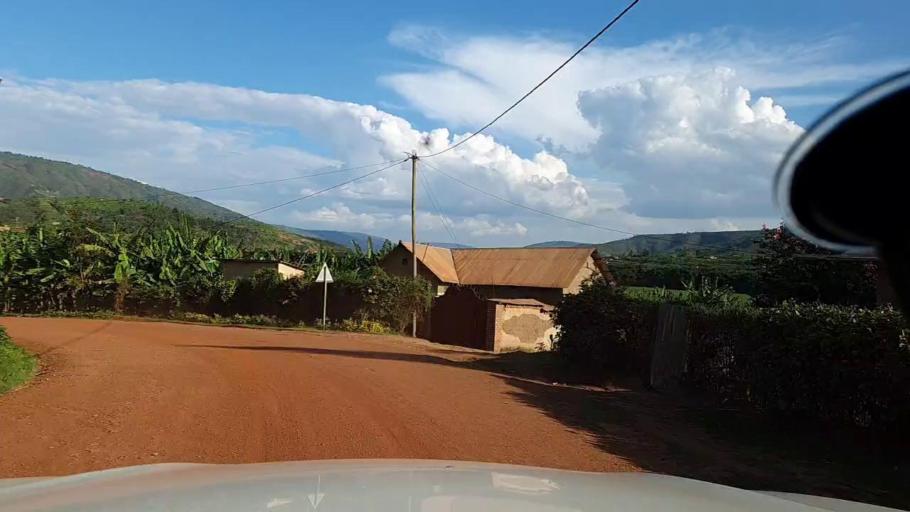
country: RW
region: Kigali
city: Kigali
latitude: -1.8644
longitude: 29.9206
